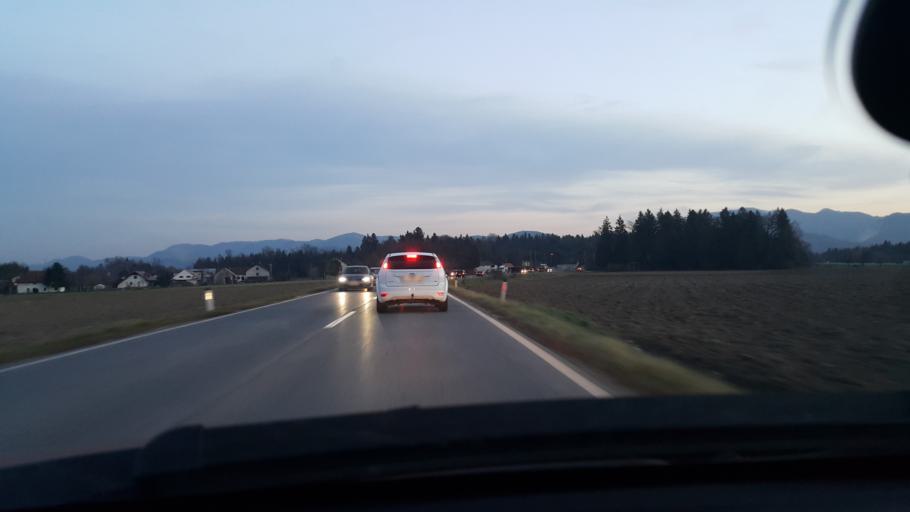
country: SI
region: Zalec
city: Zalec
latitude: 46.2742
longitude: 15.1886
